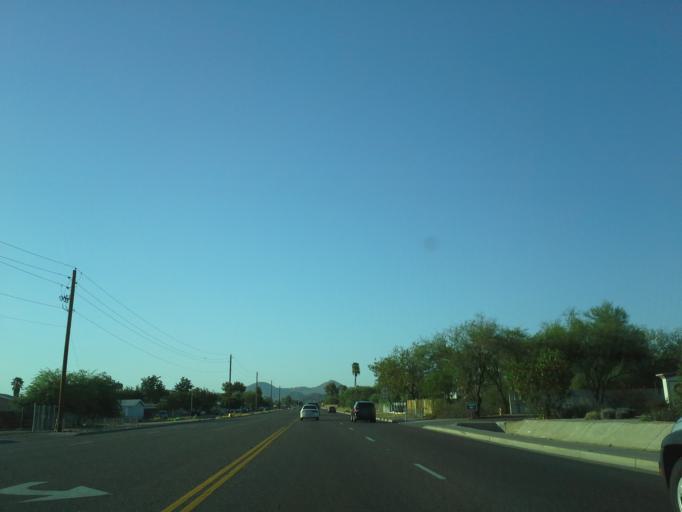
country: US
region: Arizona
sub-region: Pinal County
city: Apache Junction
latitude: 33.4083
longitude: -111.6327
